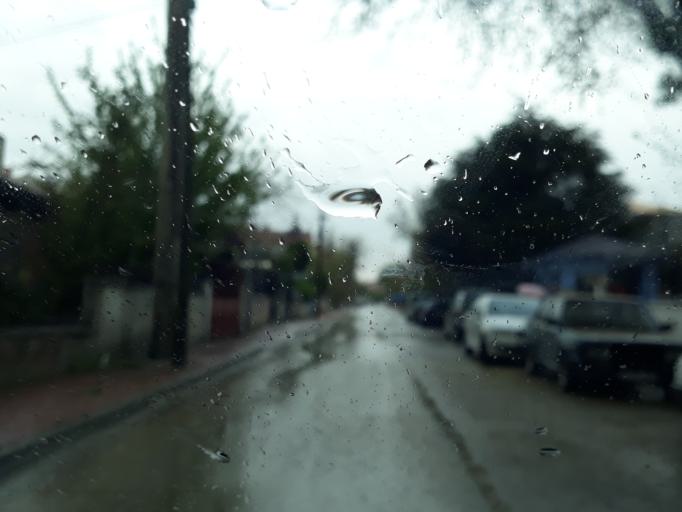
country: TR
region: Konya
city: Selcuklu
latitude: 37.9120
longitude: 32.4942
